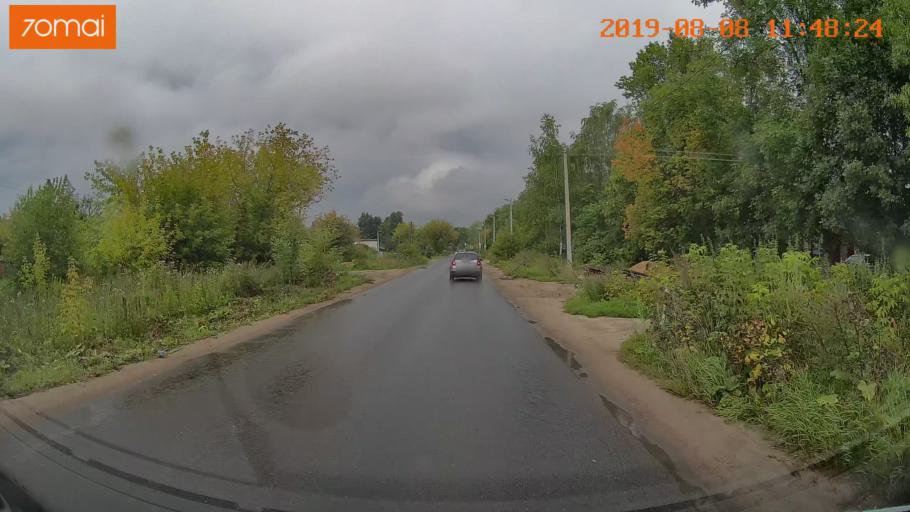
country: RU
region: Ivanovo
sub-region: Gorod Ivanovo
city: Ivanovo
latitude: 56.9726
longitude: 40.9837
